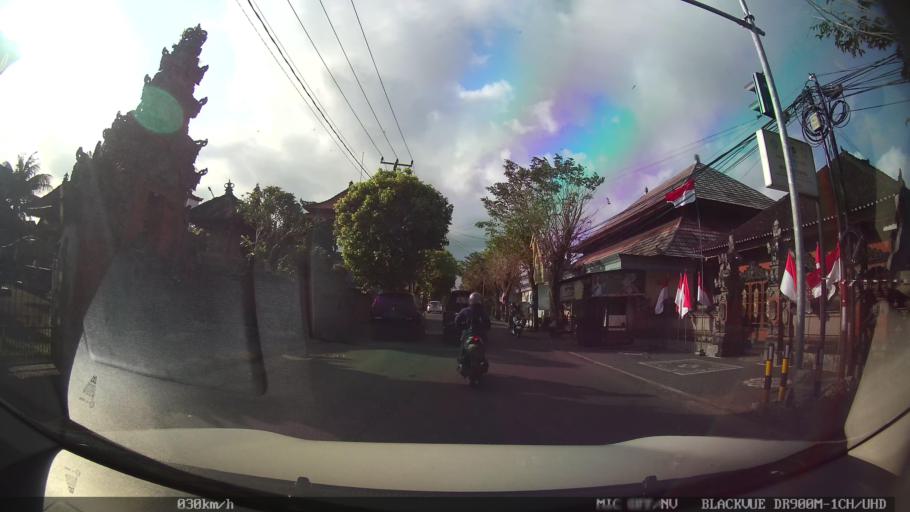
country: ID
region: Bali
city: Banjar Sedang
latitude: -8.5719
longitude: 115.2377
